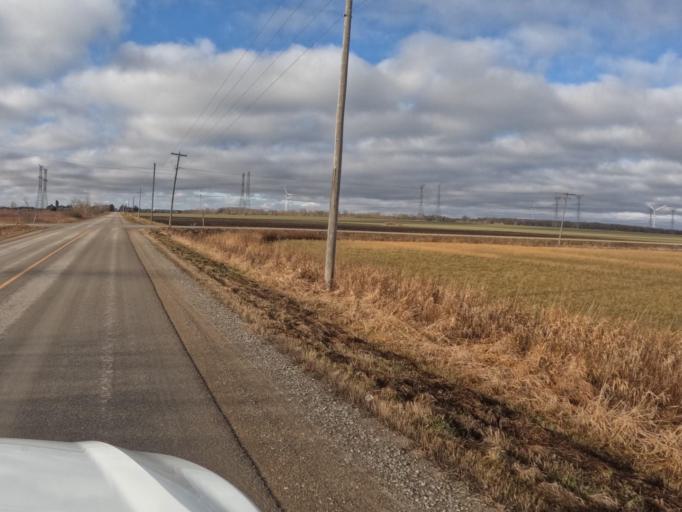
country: CA
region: Ontario
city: Shelburne
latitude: 43.8946
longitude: -80.3367
